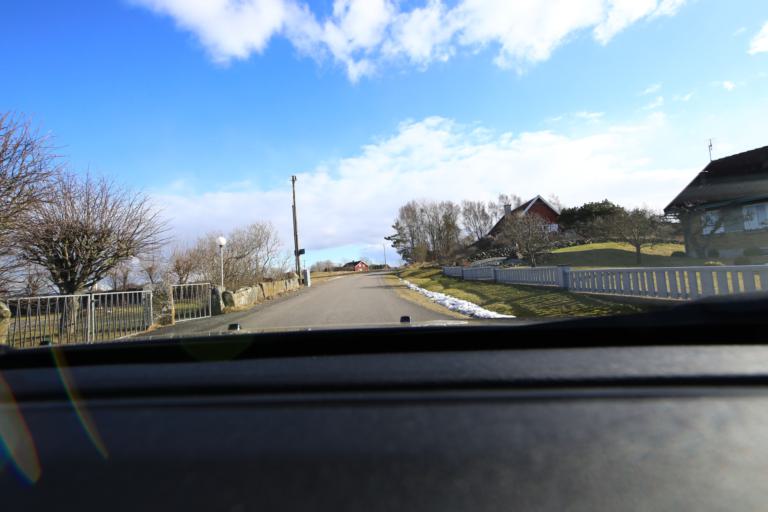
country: SE
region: Halland
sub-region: Kungsbacka Kommun
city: Frillesas
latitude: 57.2290
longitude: 12.1344
